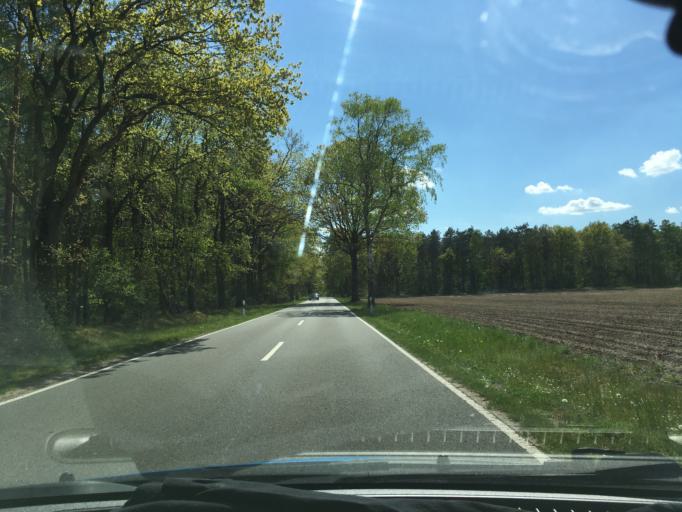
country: DE
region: Lower Saxony
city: Zernien
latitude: 53.0573
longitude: 10.8833
